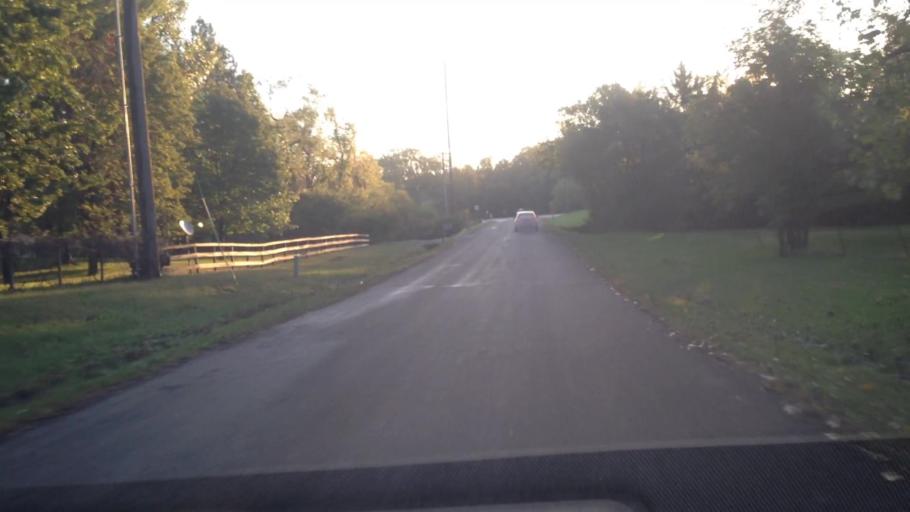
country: US
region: Kansas
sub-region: Johnson County
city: De Soto
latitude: 38.9567
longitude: -94.9876
